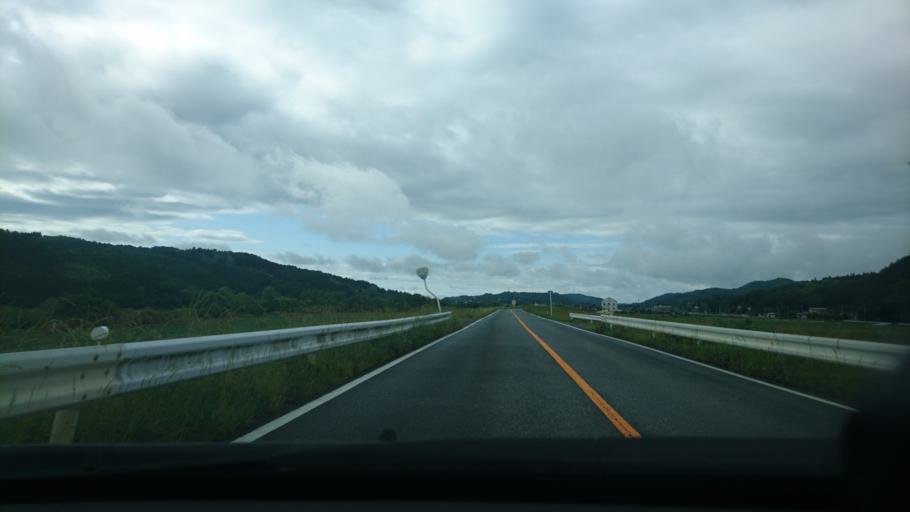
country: JP
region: Miyagi
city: Wakuya
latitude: 38.6353
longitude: 141.2893
